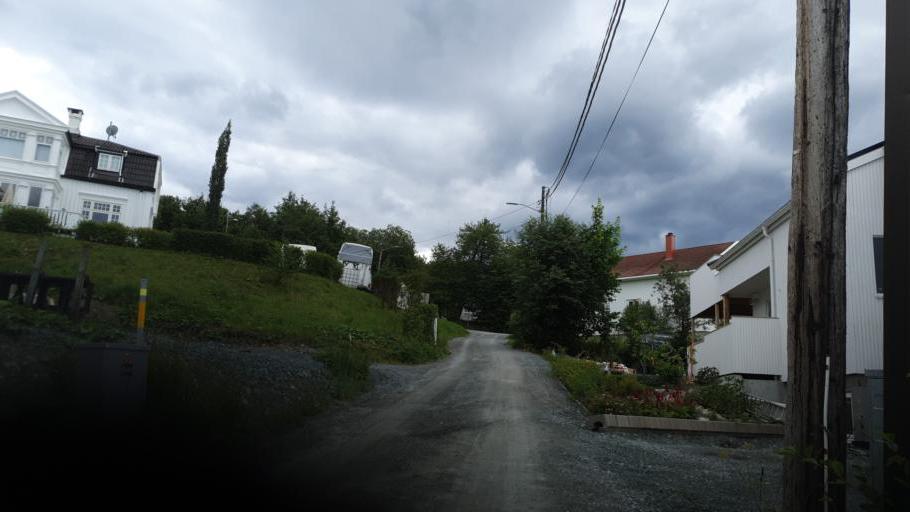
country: NO
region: Sor-Trondelag
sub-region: Malvik
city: Malvik
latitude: 63.4399
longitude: 10.5975
